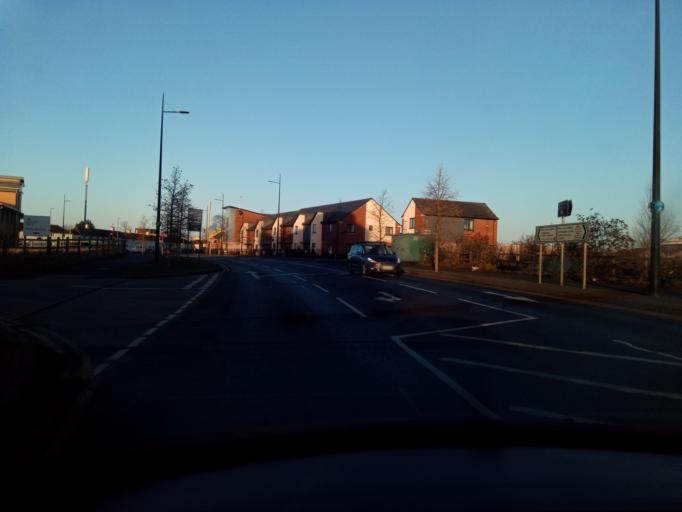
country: GB
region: England
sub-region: Leicestershire
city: Loughborough
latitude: 52.7809
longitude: -1.1997
